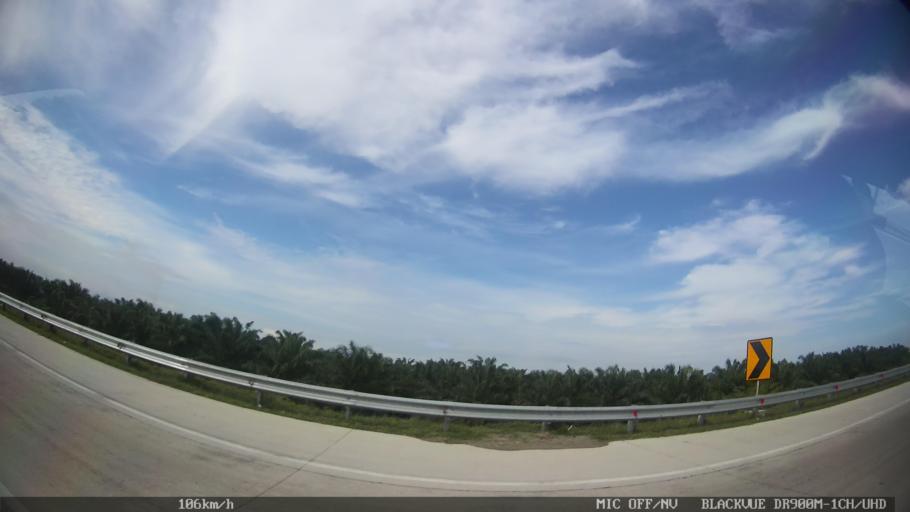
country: ID
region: North Sumatra
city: Binjai
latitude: 3.6516
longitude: 98.5379
